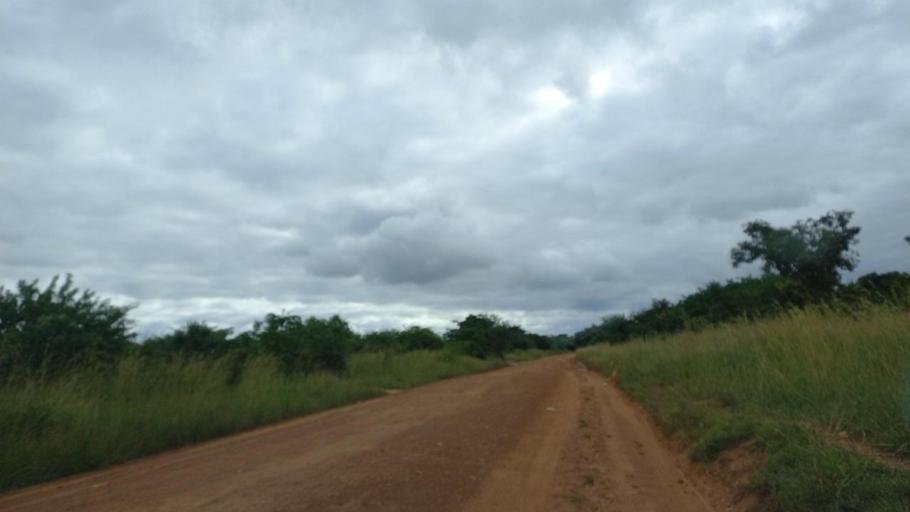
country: ZM
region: Lusaka
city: Chongwe
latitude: -15.4564
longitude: 28.8679
